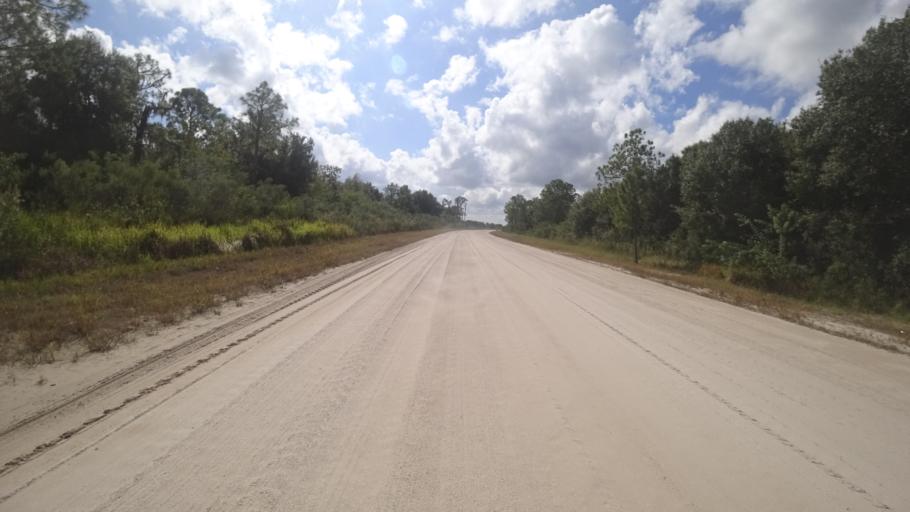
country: US
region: Florida
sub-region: Hillsborough County
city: Wimauma
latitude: 27.4504
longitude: -82.1827
